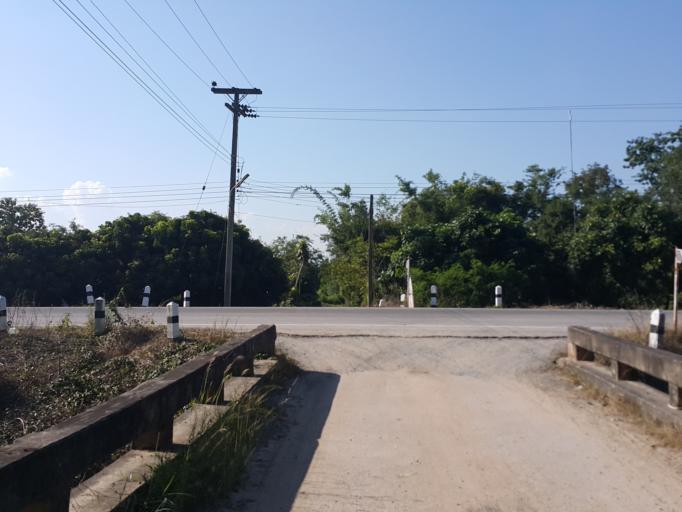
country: TH
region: Chiang Mai
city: Mae On
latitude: 18.7963
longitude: 99.1810
